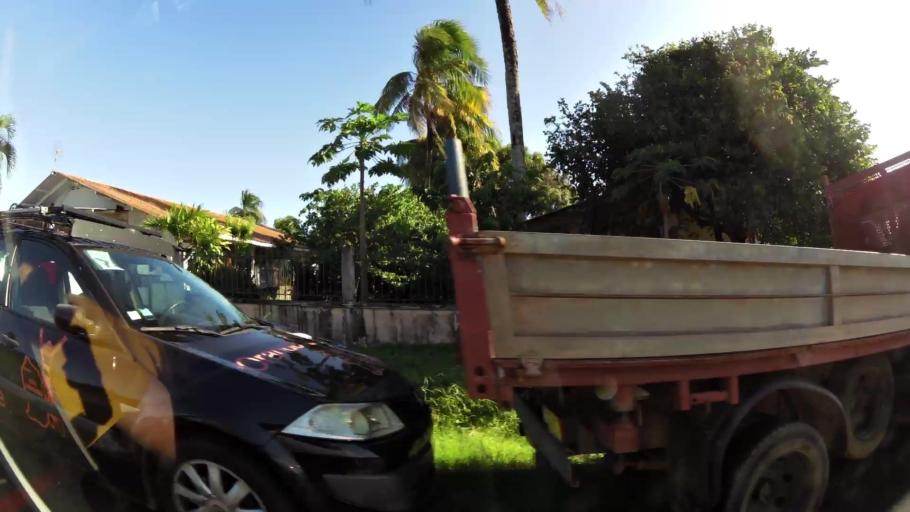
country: GF
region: Guyane
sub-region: Guyane
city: Remire-Montjoly
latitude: 4.8981
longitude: -52.2768
